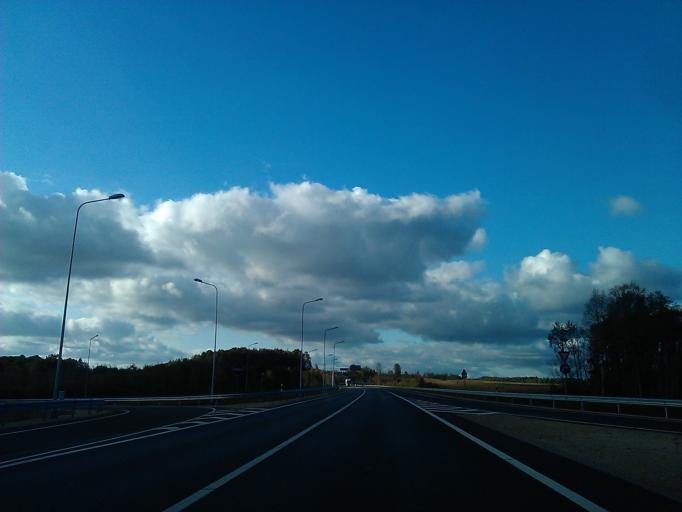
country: LV
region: Skriveri
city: Skriveri
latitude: 56.7653
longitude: 25.0987
